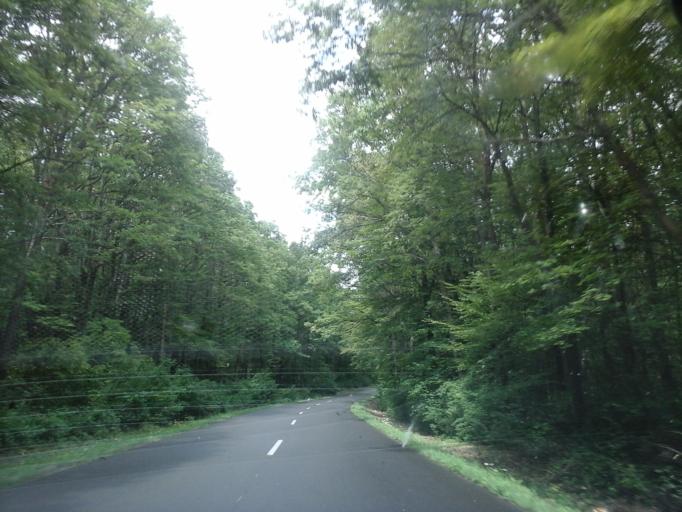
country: HU
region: Borsod-Abauj-Zemplen
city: Putnok
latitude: 48.4405
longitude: 20.4851
